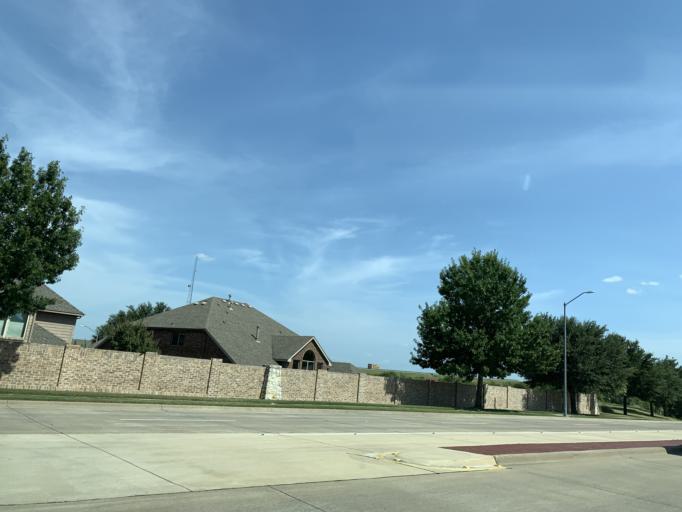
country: US
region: Texas
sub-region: Dallas County
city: Cedar Hill
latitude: 32.6475
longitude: -97.0070
